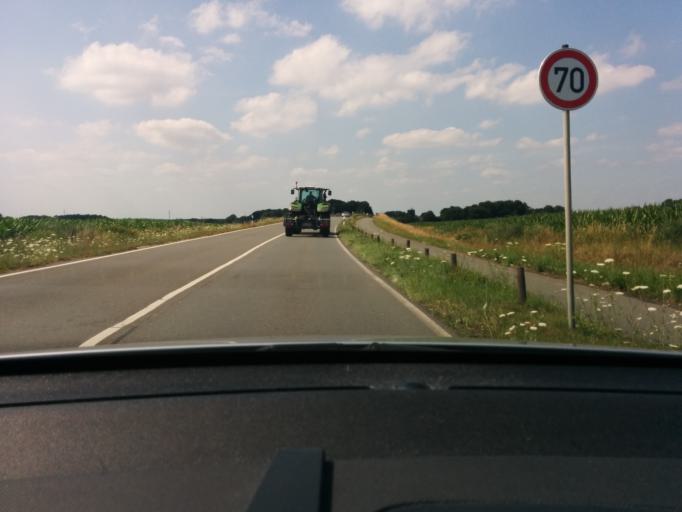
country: DE
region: North Rhine-Westphalia
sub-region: Regierungsbezirk Munster
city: Steinfurt
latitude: 52.1680
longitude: 7.2933
